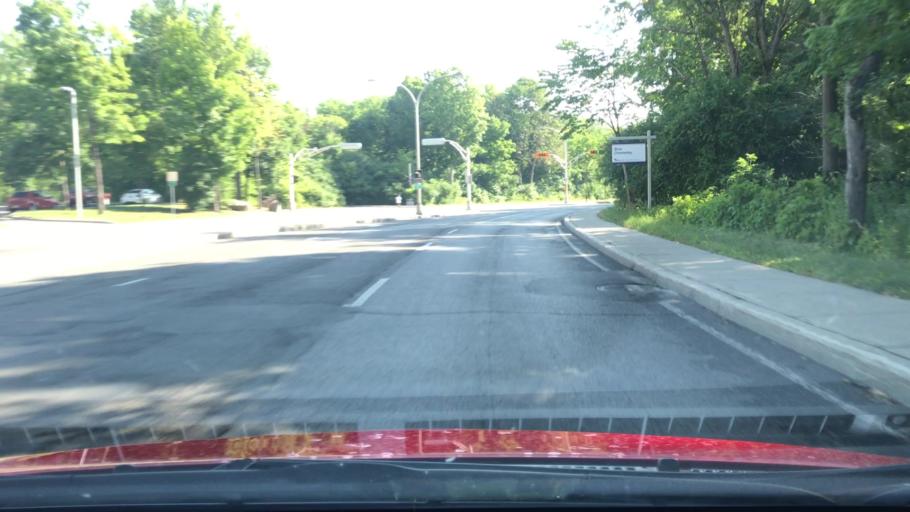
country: CA
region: Quebec
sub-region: Laval
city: Laval
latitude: 45.5482
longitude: -73.7336
